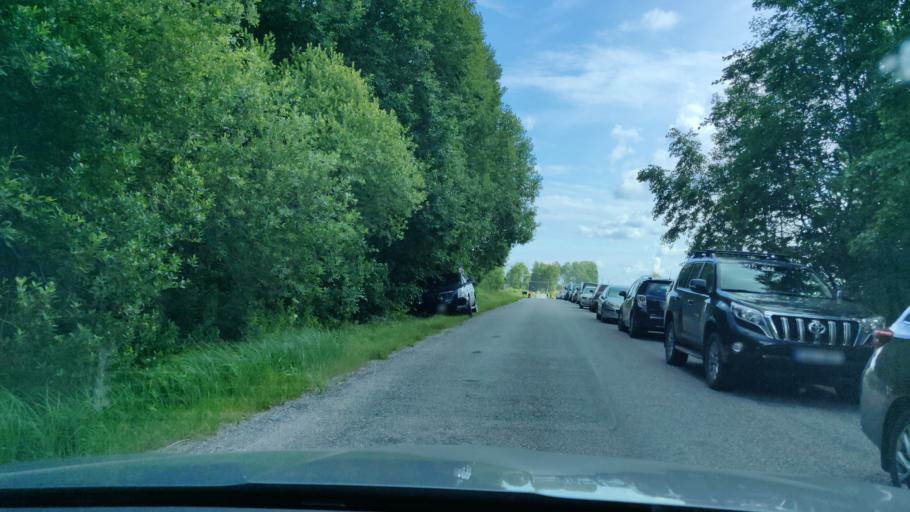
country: EE
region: Tartu
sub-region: Elva linn
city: Elva
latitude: 58.0259
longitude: 26.3424
